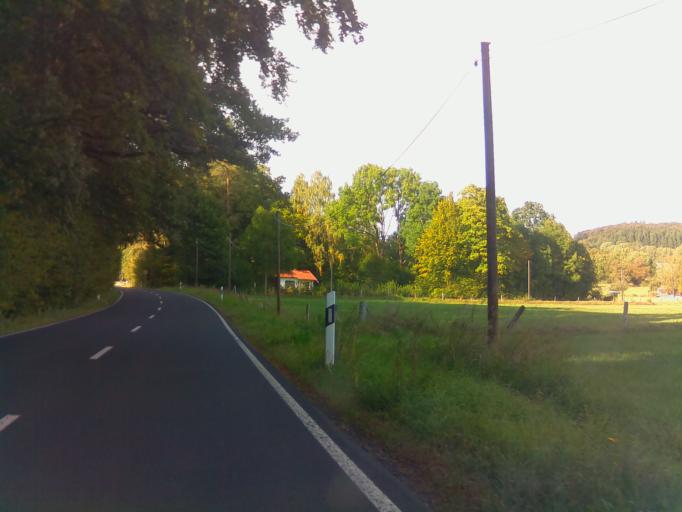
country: DE
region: Hesse
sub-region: Regierungsbezirk Kassel
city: Poppenhausen
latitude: 50.5181
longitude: 9.8686
